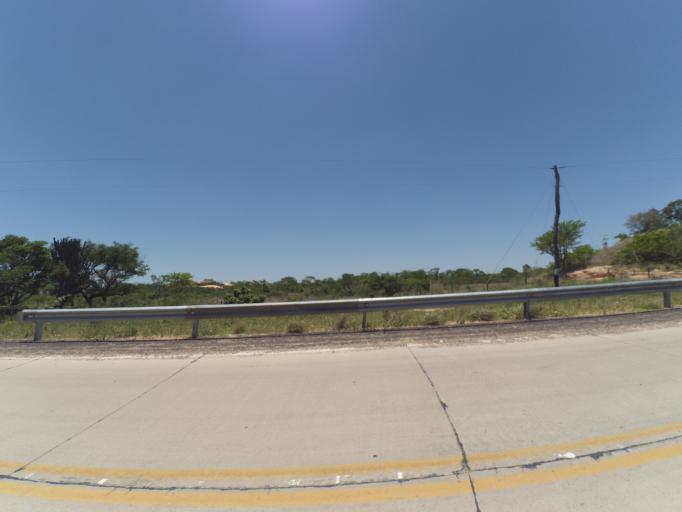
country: BO
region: Santa Cruz
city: Santa Cruz de la Sierra
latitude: -17.8156
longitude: -63.2835
